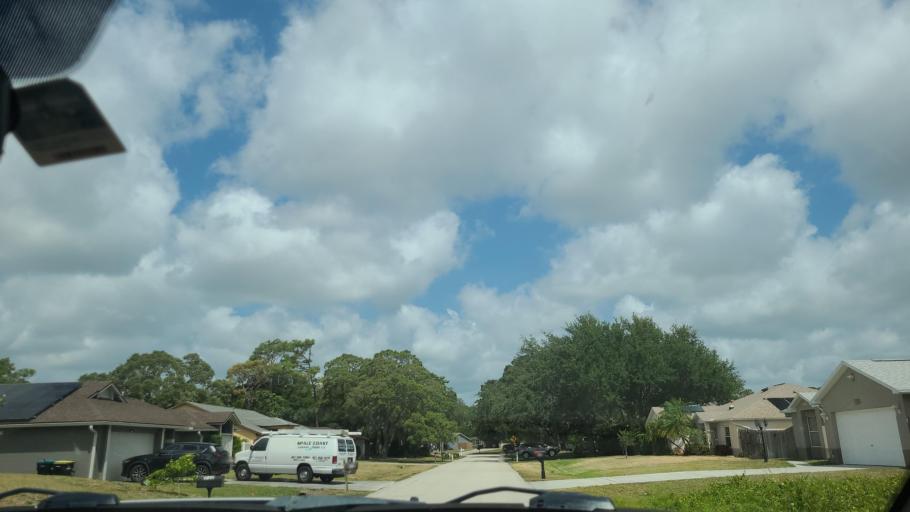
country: US
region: Florida
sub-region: Brevard County
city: Palm Bay
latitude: 28.0045
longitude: -80.6488
